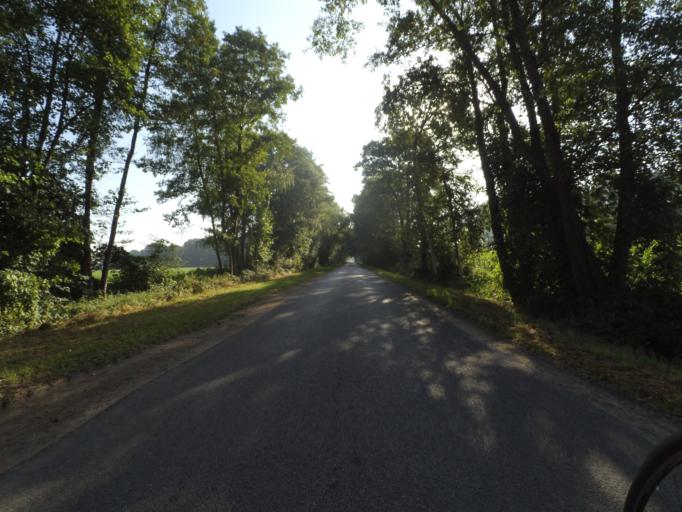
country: DE
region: Lower Saxony
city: Ohne
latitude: 52.2746
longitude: 7.2552
